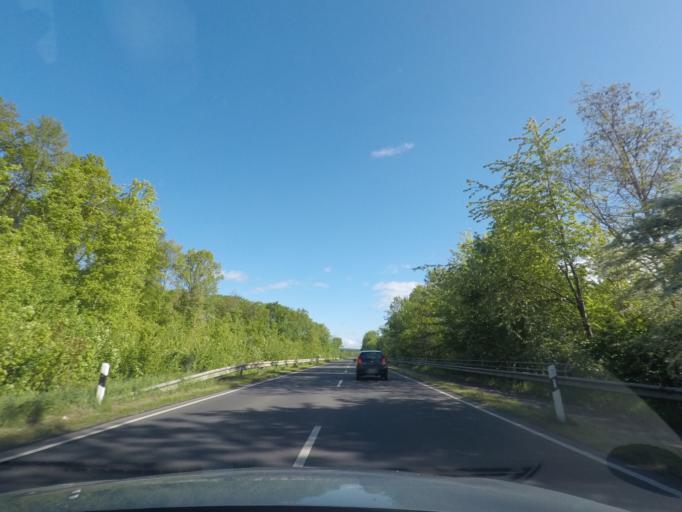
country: DE
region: Lower Saxony
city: Wolsdorf
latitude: 52.1809
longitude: 10.9757
